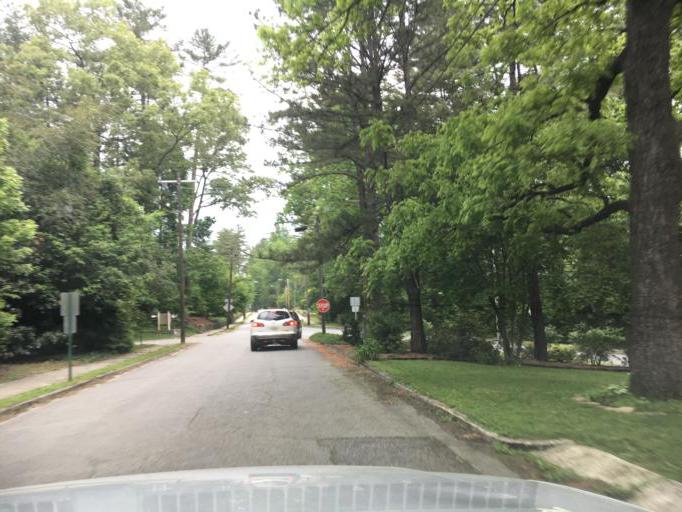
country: US
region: North Carolina
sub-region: Transylvania County
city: Brevard
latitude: 35.2284
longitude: -82.7280
